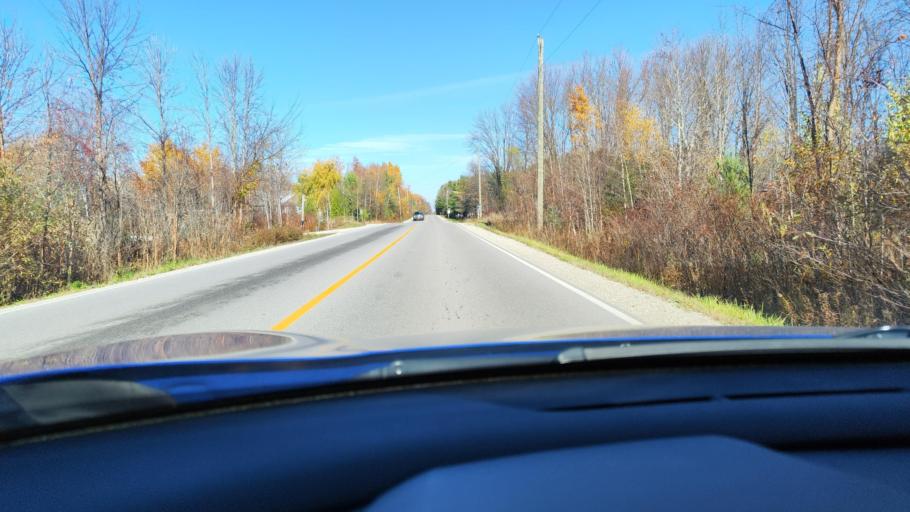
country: CA
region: Ontario
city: Wasaga Beach
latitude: 44.4042
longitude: -80.0586
